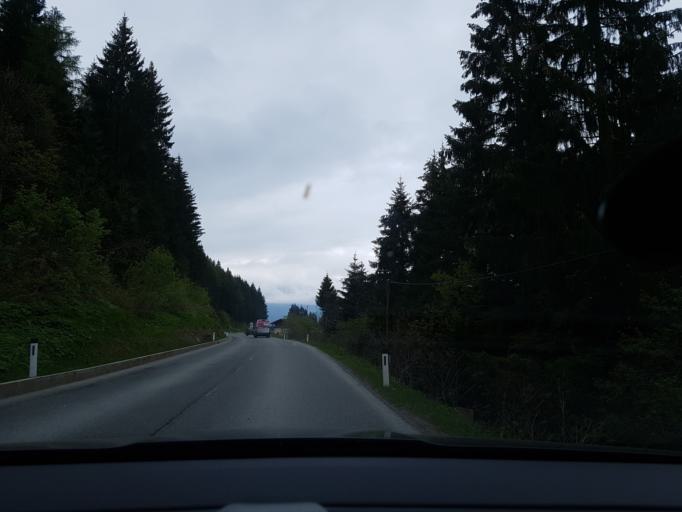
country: AT
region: Tyrol
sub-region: Politischer Bezirk Schwaz
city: Gerlosberg
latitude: 47.2112
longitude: 11.9475
